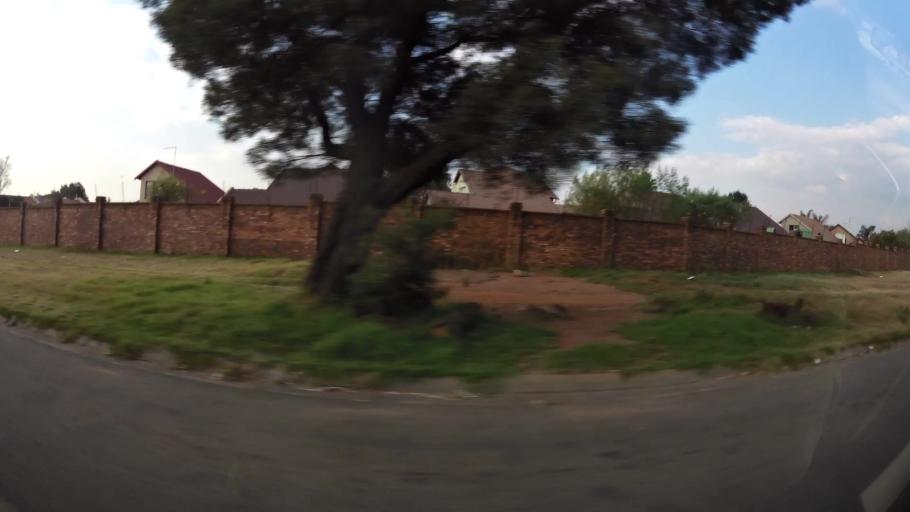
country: ZA
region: Gauteng
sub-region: Ekurhuleni Metropolitan Municipality
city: Benoni
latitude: -26.1430
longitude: 28.2967
